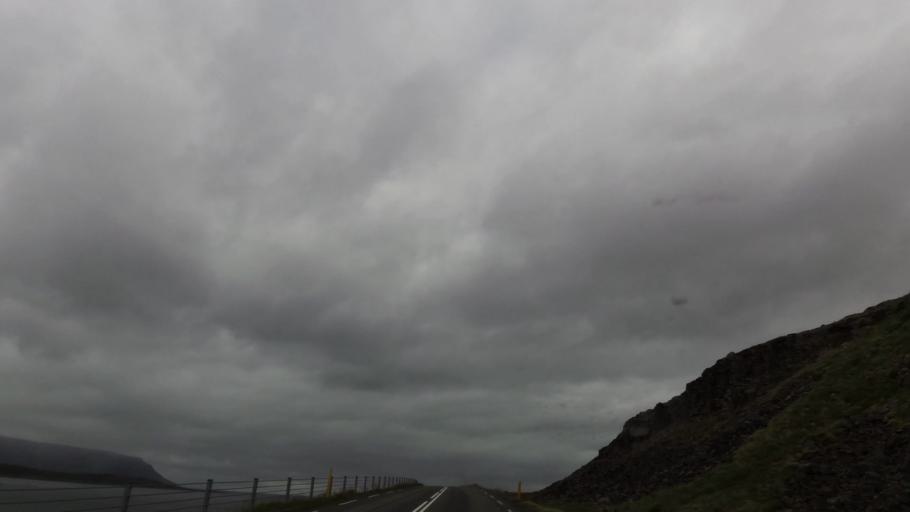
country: IS
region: Westfjords
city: Isafjoerdur
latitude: 65.9983
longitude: -22.7809
